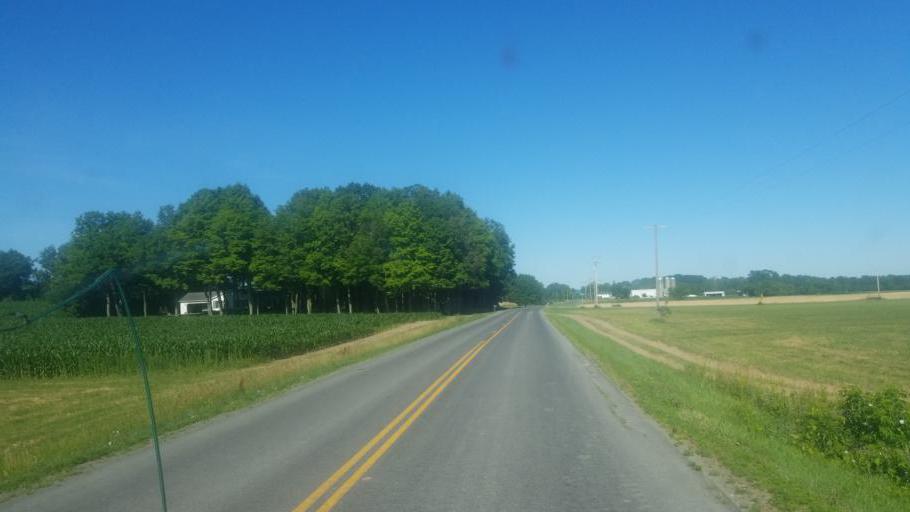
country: US
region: New York
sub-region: Ontario County
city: Canandaigua
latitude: 42.8358
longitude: -77.1981
